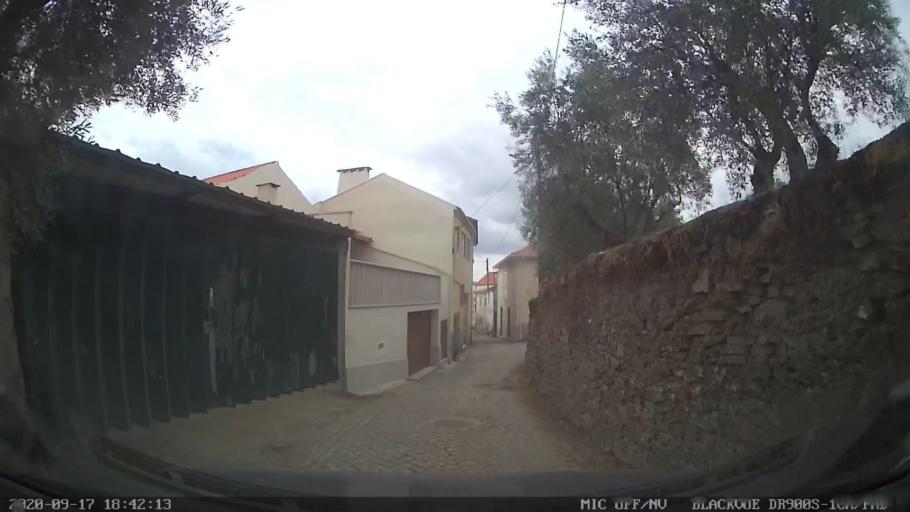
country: PT
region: Vila Real
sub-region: Sabrosa
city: Sabrosa
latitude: 41.2430
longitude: -7.5786
